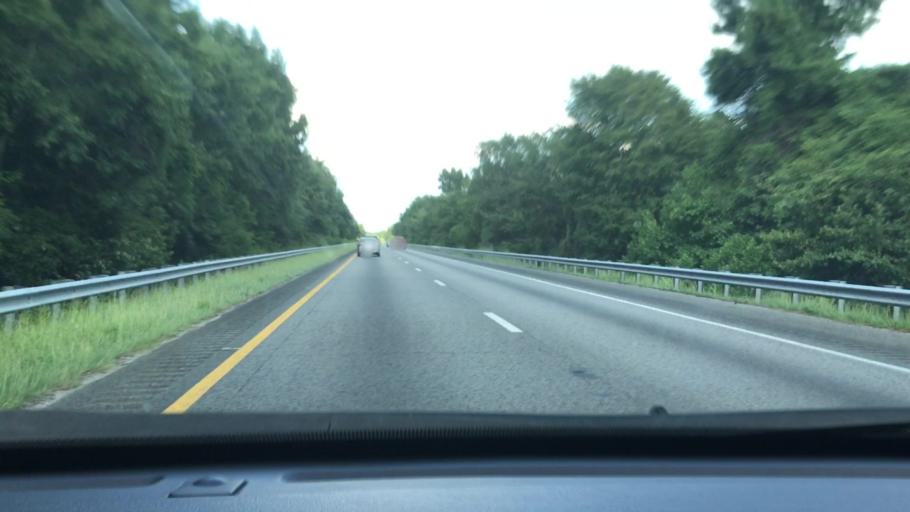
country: US
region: South Carolina
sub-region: Florence County
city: Florence
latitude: 34.2850
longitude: -79.6714
